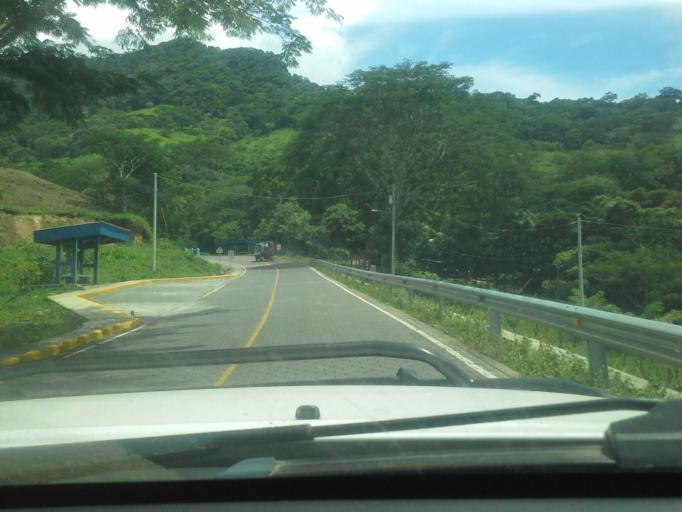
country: NI
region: Boaco
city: San Jose de los Remates
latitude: 12.6934
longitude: -85.7457
